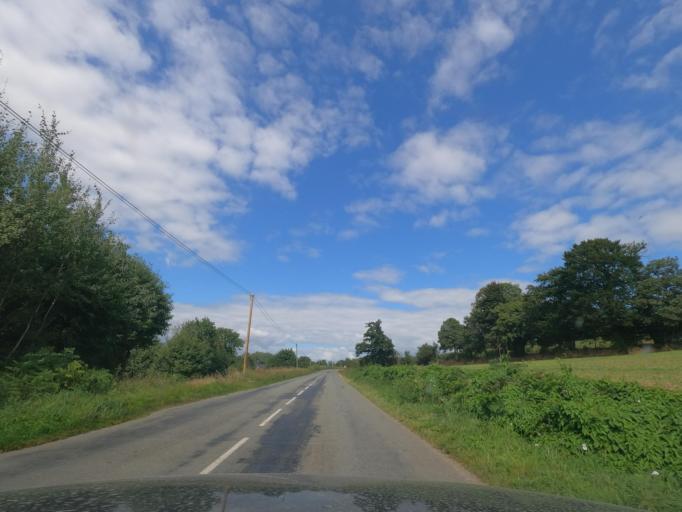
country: FR
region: Pays de la Loire
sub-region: Departement de la Mayenne
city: Landivy
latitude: 48.4701
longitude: -1.0467
